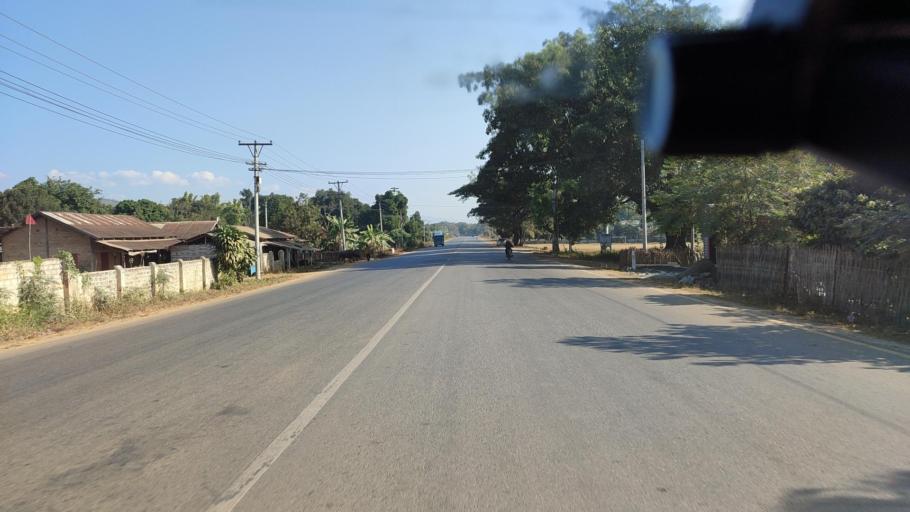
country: MM
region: Shan
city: Lashio
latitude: 23.2377
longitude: 97.9129
